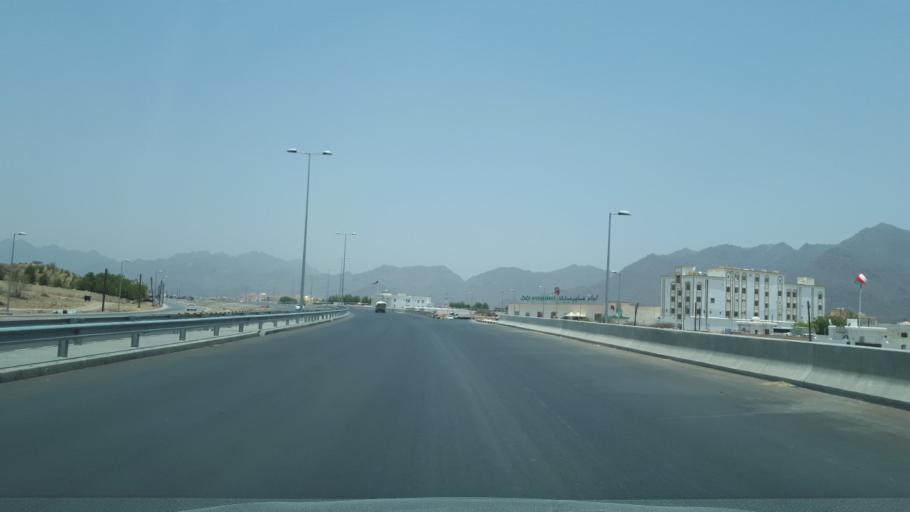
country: OM
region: Al Batinah
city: Rustaq
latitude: 23.4365
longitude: 57.4185
